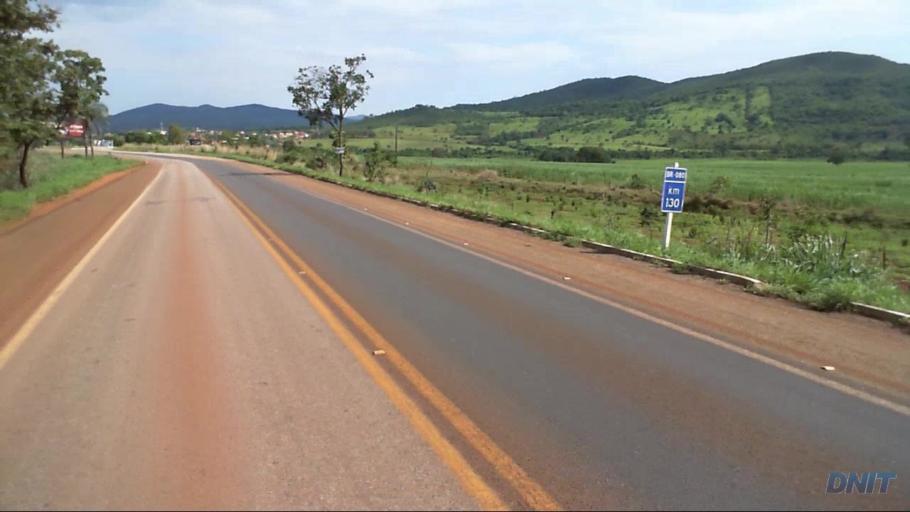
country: BR
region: Goias
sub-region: Barro Alto
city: Barro Alto
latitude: -14.9912
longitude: -48.9083
